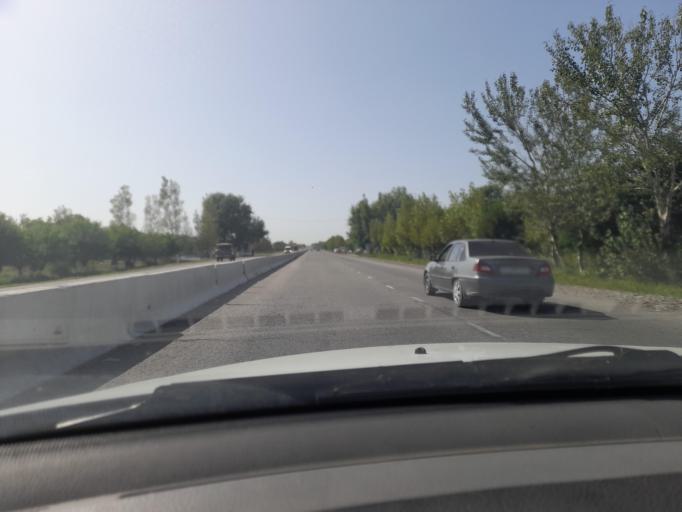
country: UZ
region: Samarqand
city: Chelak
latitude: 39.8455
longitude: 66.8104
